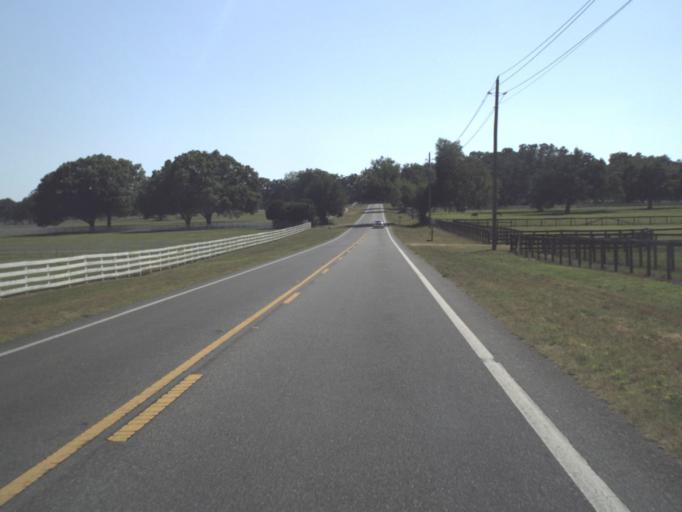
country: US
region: Florida
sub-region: Marion County
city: Dunnellon
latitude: 29.1742
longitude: -82.3291
